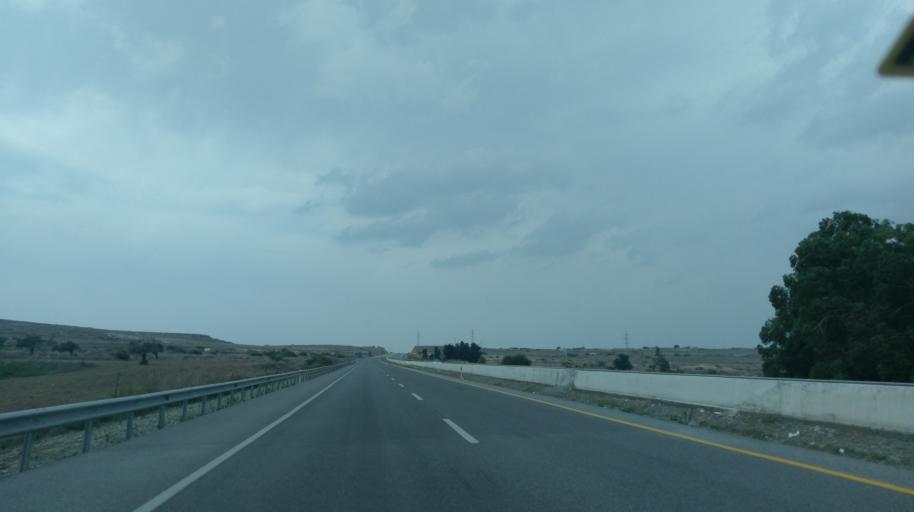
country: CY
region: Lefkosia
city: Peristerona
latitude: 35.1956
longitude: 33.0839
